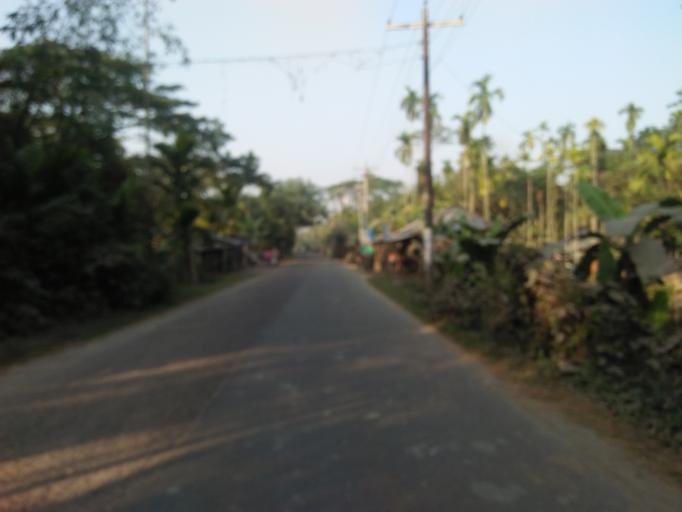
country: BD
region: Barisal
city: Bhola
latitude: 22.7417
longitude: 90.6342
